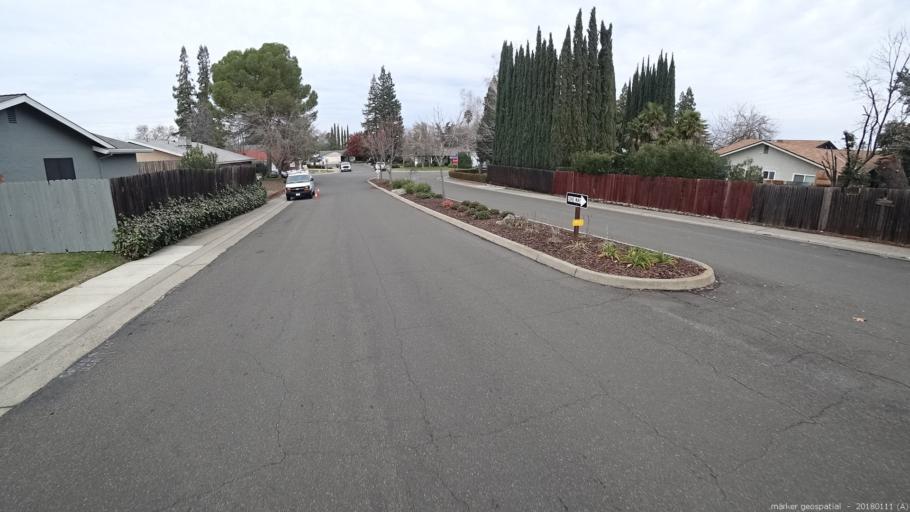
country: US
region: California
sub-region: Sacramento County
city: Fair Oaks
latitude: 38.6176
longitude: -121.2786
